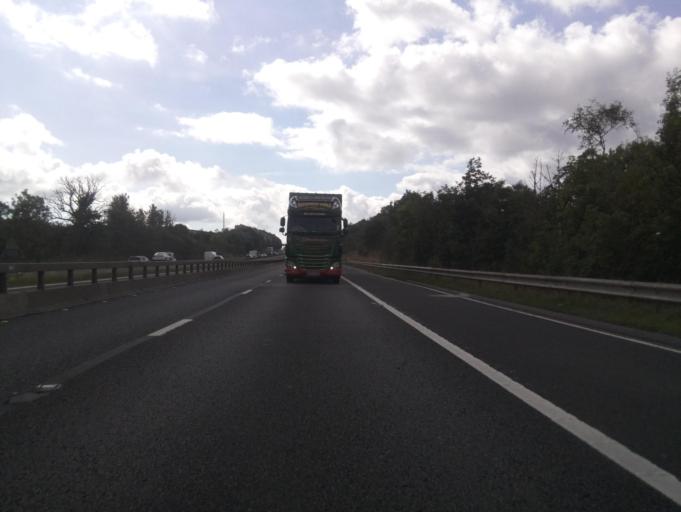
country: GB
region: England
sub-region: Cumbria
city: Kendal
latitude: 54.2908
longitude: -2.6564
